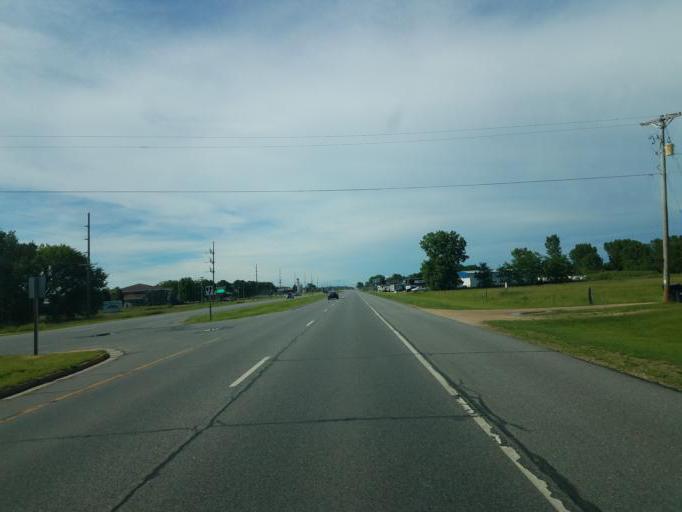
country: US
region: Wisconsin
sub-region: Monroe County
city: Tomah
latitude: 43.9959
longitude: -90.5047
